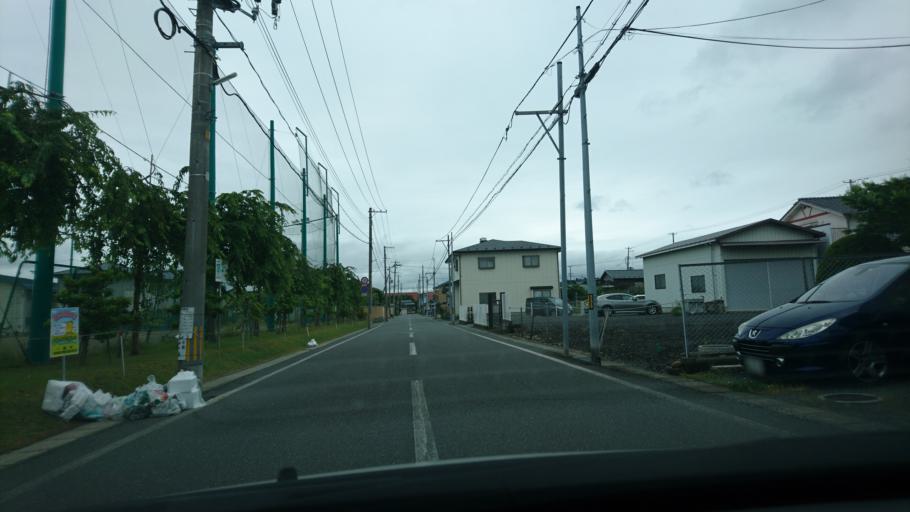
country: JP
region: Iwate
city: Ichinoseki
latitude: 38.9344
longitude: 141.1355
